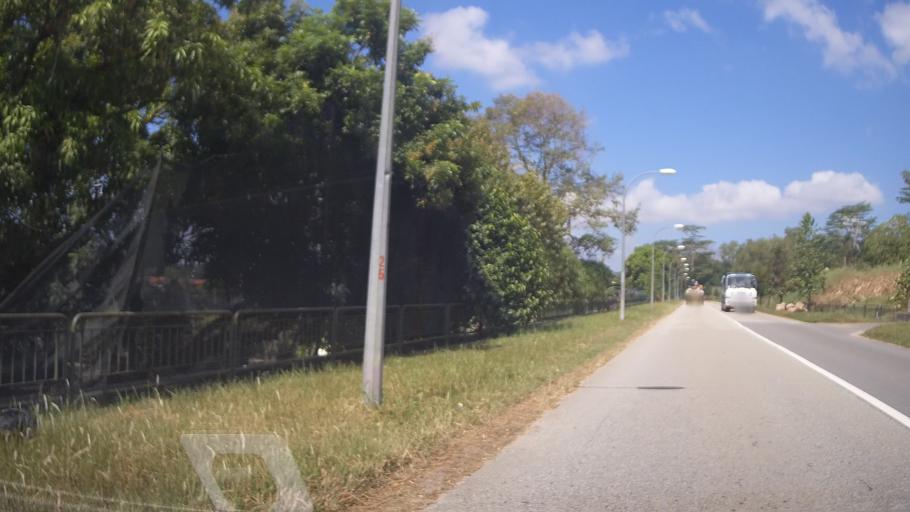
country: MY
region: Johor
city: Johor Bahru
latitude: 1.4327
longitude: 103.7162
